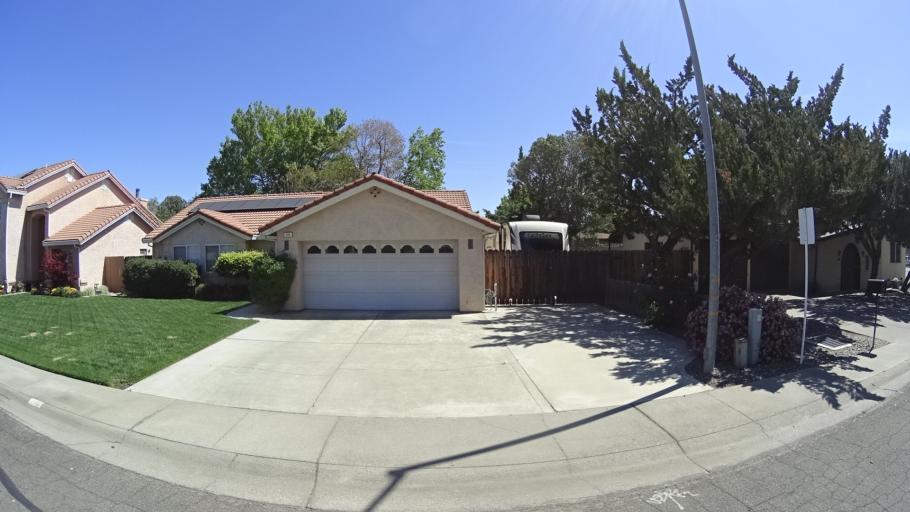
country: US
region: California
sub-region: Glenn County
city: Orland
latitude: 39.7512
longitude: -122.1804
